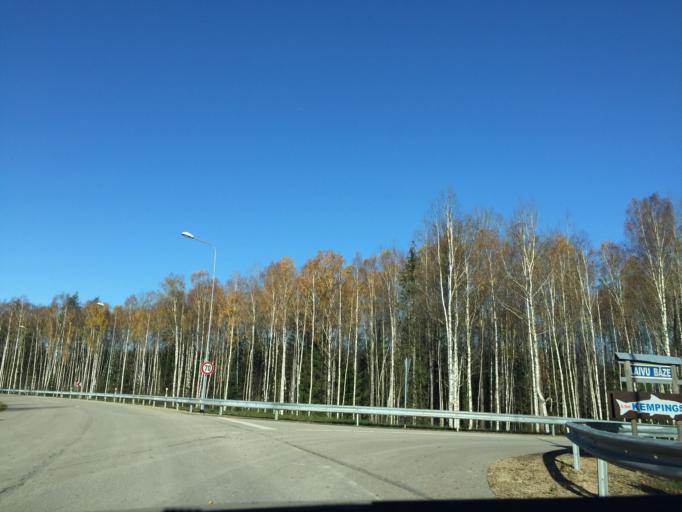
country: LV
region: Aizkraukles Rajons
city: Aizkraukle
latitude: 56.7038
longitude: 25.2829
